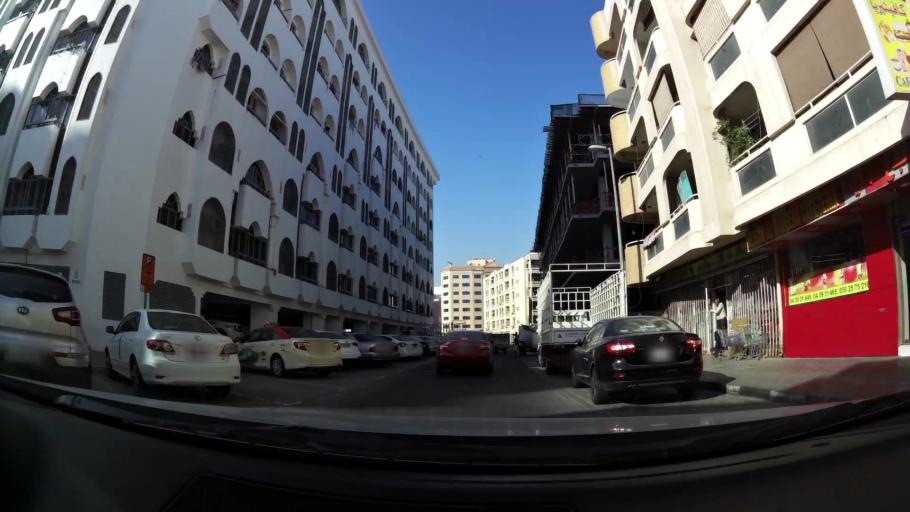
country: AE
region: Ash Shariqah
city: Sharjah
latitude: 25.2581
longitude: 55.2866
